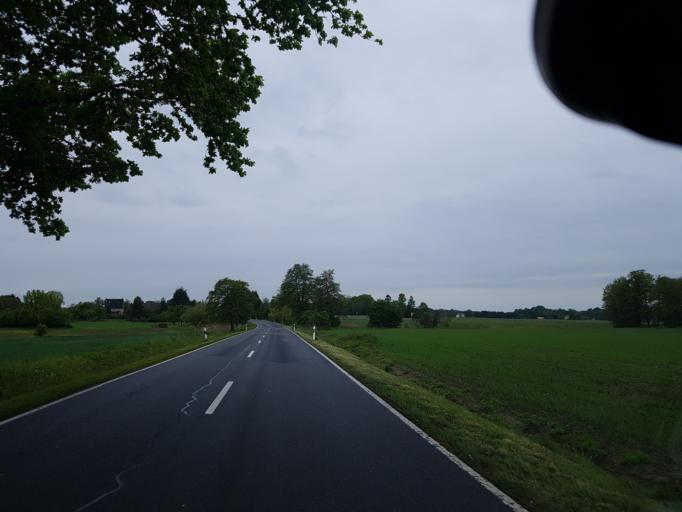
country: DE
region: Saxony
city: Gross Duben
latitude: 51.6374
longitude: 14.5266
